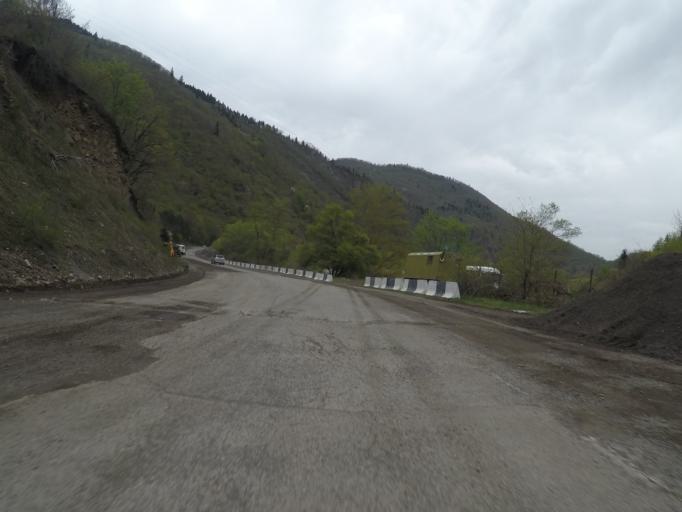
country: GE
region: Samtskhe-Javakheti
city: Borjomi
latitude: 41.9087
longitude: 43.4721
